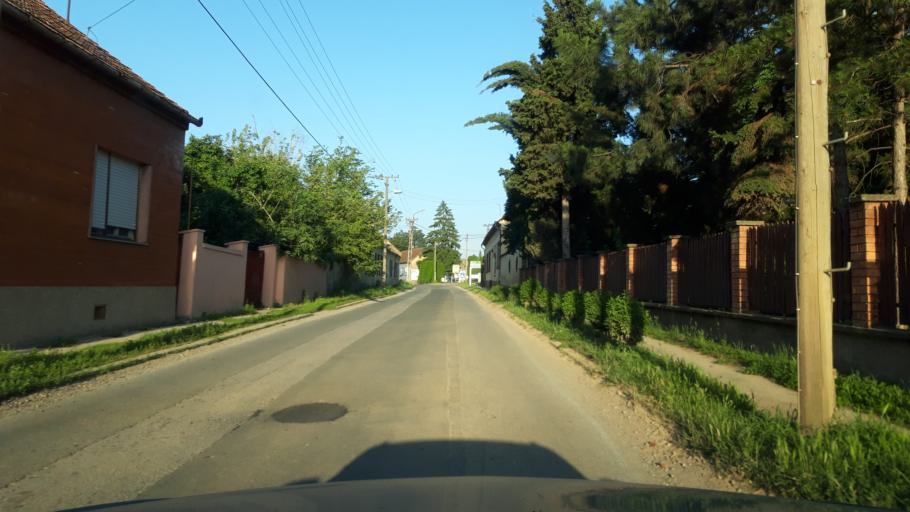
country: RS
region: Autonomna Pokrajina Vojvodina
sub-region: Juznobacki Okrug
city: Beocin
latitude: 45.2203
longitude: 19.6612
